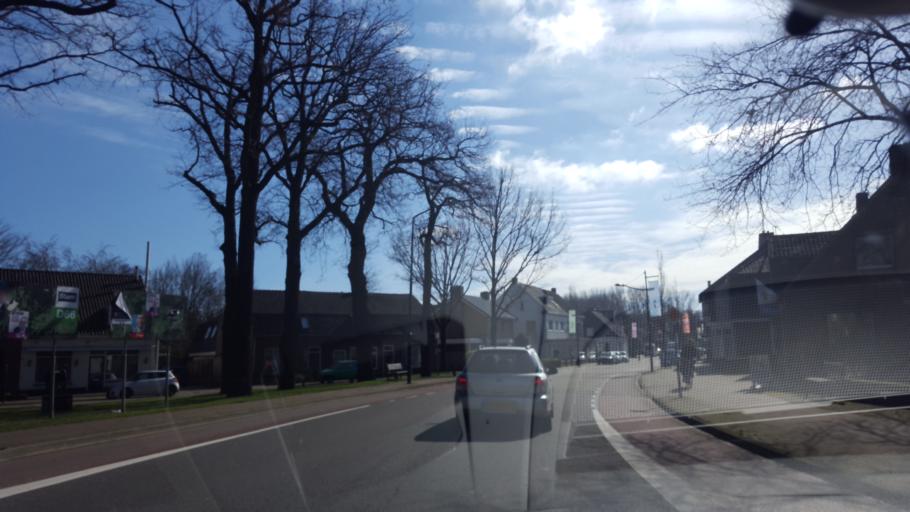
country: NL
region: North Brabant
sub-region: Gemeente Heeze-Leende
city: Heeze
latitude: 51.3851
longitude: 5.5793
